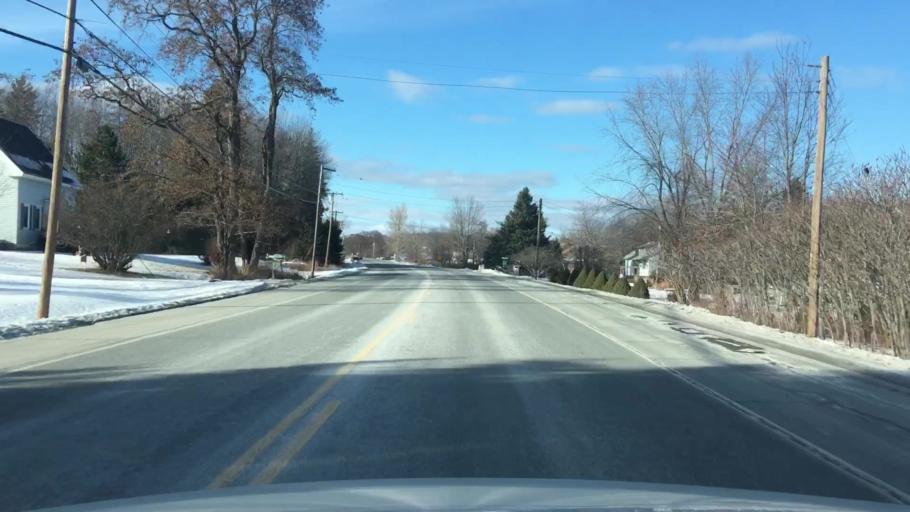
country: US
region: Maine
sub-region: Penobscot County
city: Eddington
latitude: 44.8219
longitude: -68.6499
